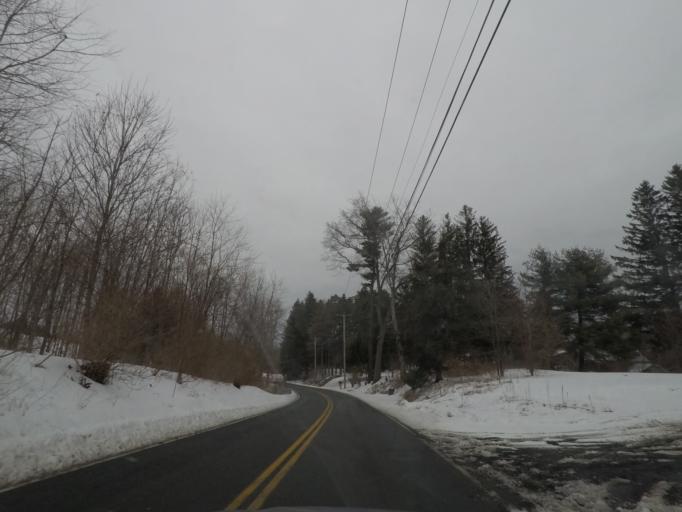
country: US
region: New York
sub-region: Schenectady County
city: Niskayuna
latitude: 42.7679
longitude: -73.8056
